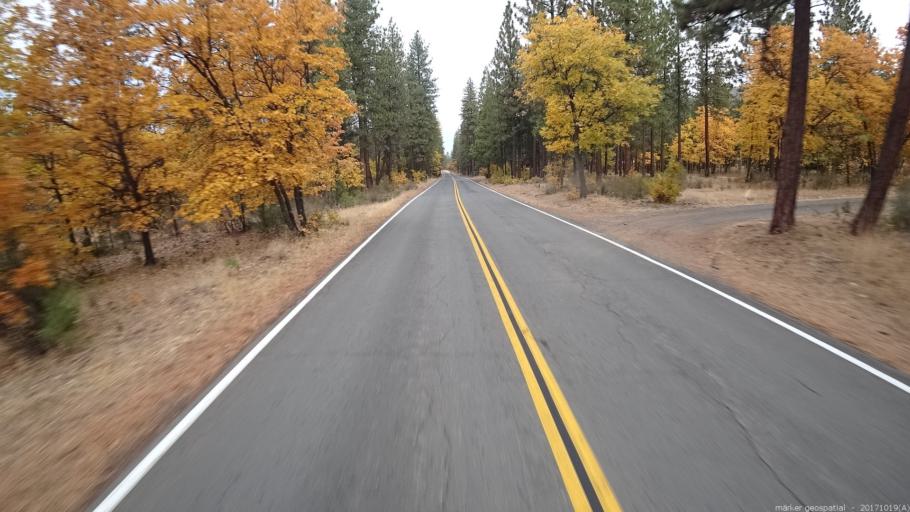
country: US
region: California
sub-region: Shasta County
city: Burney
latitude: 41.1404
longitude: -121.3465
